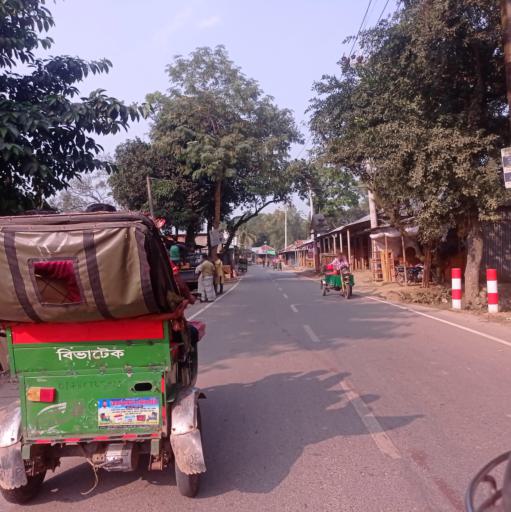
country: BD
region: Dhaka
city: Bhairab Bazar
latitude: 24.0822
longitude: 90.8492
